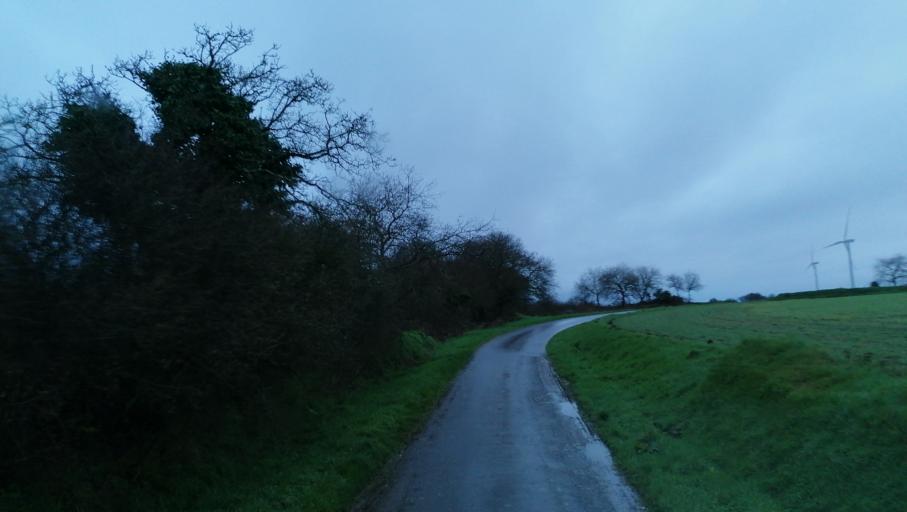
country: FR
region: Brittany
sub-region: Departement des Cotes-d'Armor
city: Lanrodec
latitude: 48.4822
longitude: -2.9991
